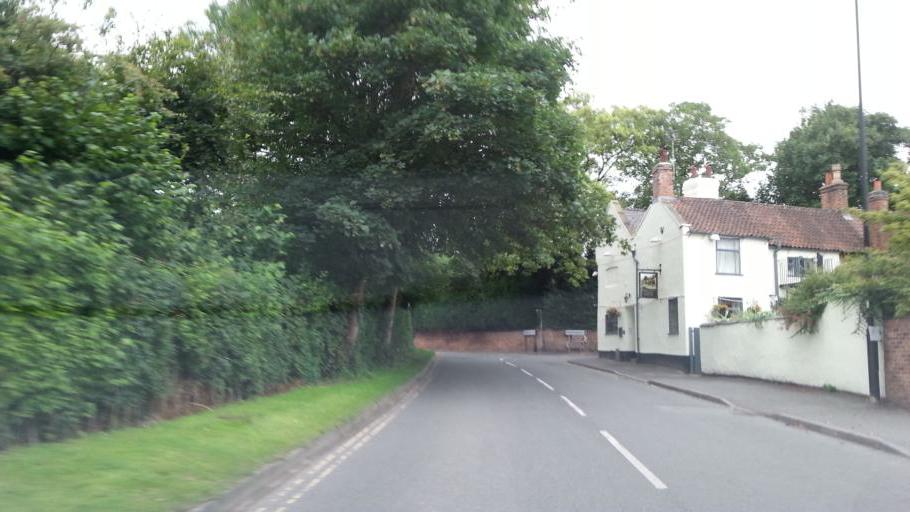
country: GB
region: England
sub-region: Nottinghamshire
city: Southwell
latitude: 53.0760
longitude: -0.9444
